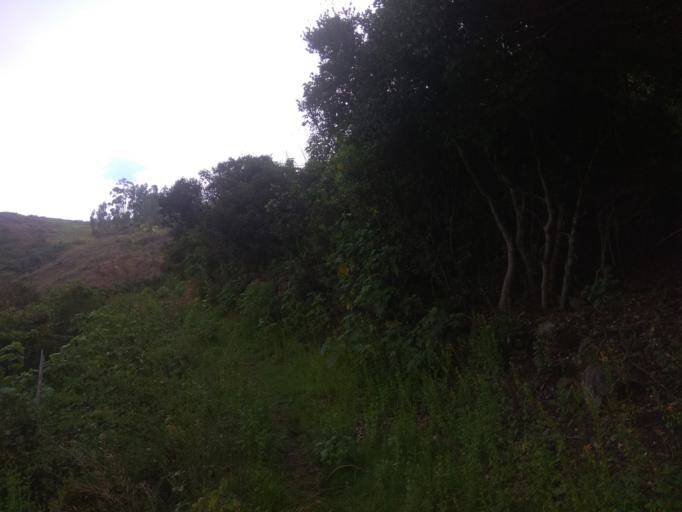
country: CO
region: Boyaca
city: Socha Viejo
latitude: 6.0080
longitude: -72.6775
